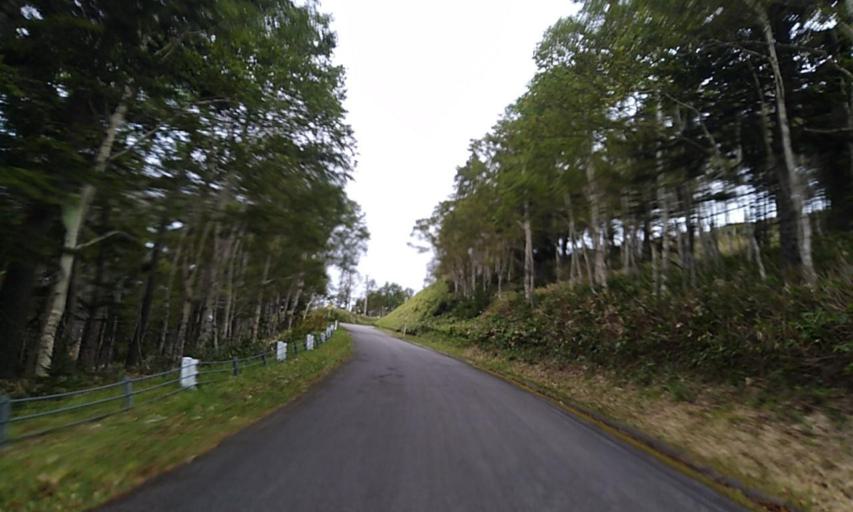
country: JP
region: Hokkaido
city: Bihoro
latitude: 43.5763
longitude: 144.2246
